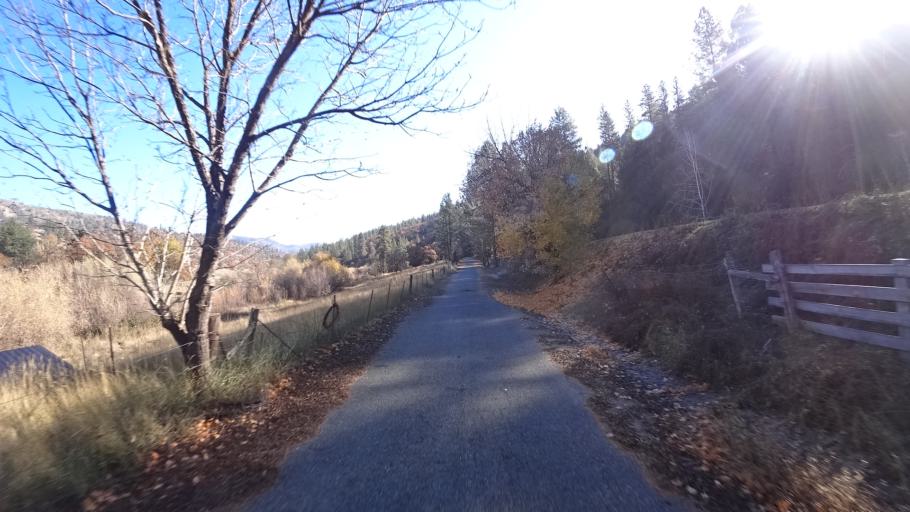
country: US
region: California
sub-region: Siskiyou County
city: Yreka
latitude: 41.8374
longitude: -122.9371
